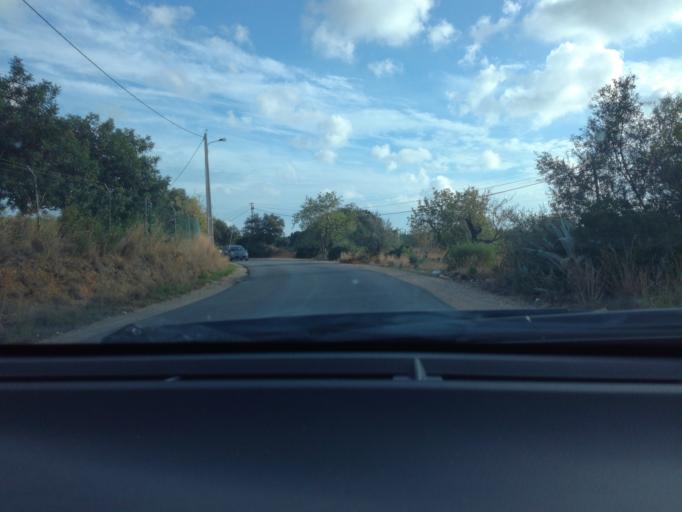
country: PT
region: Faro
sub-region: Sao Bras de Alportel
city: Sao Bras de Alportel
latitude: 37.0894
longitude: -7.8877
